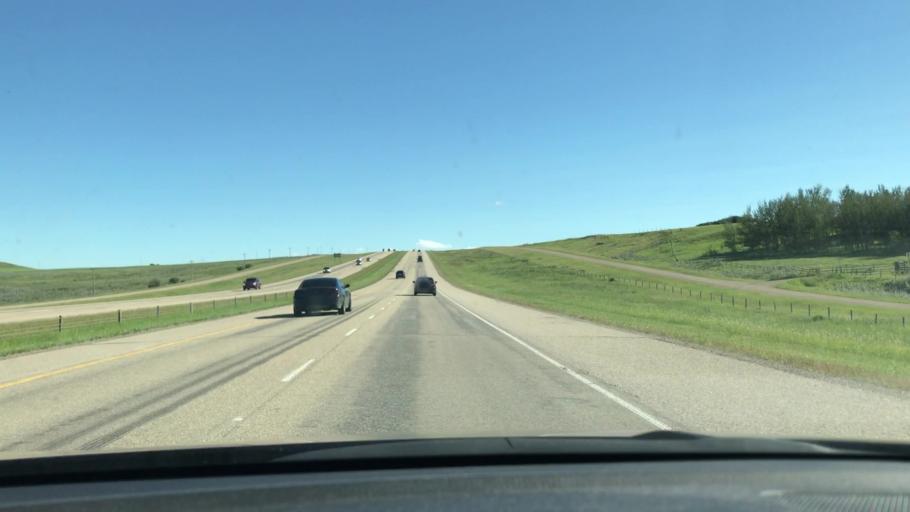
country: CA
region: Alberta
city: Carstairs
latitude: 51.5494
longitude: -114.0254
